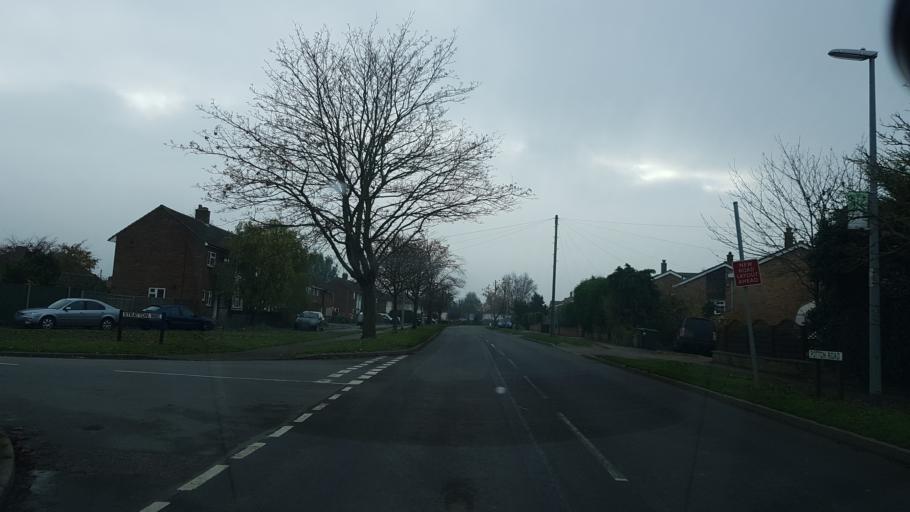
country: GB
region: England
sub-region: Central Bedfordshire
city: Biggleswade
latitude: 52.0950
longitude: -0.2524
